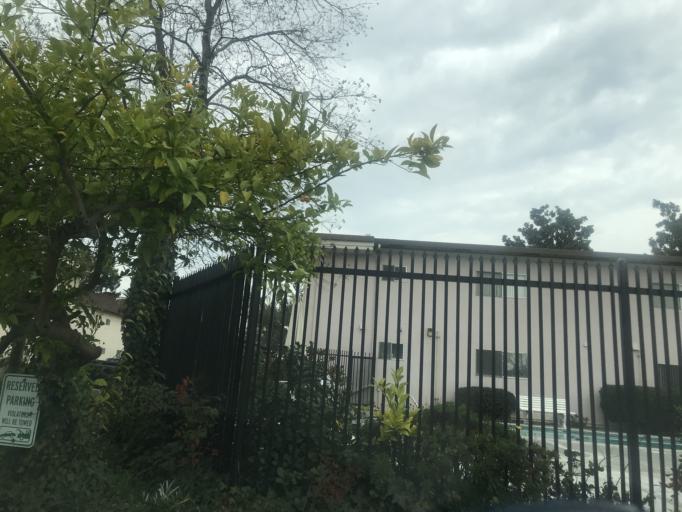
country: US
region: California
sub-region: Sacramento County
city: Arden-Arcade
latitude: 38.5830
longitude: -121.4138
